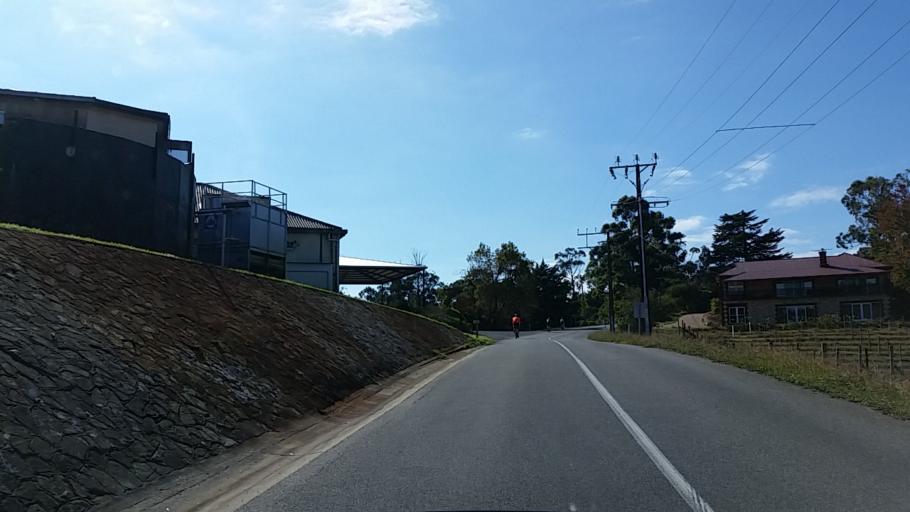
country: AU
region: South Australia
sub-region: Adelaide Hills
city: Adelaide Hills
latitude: -34.9435
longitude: 138.7274
